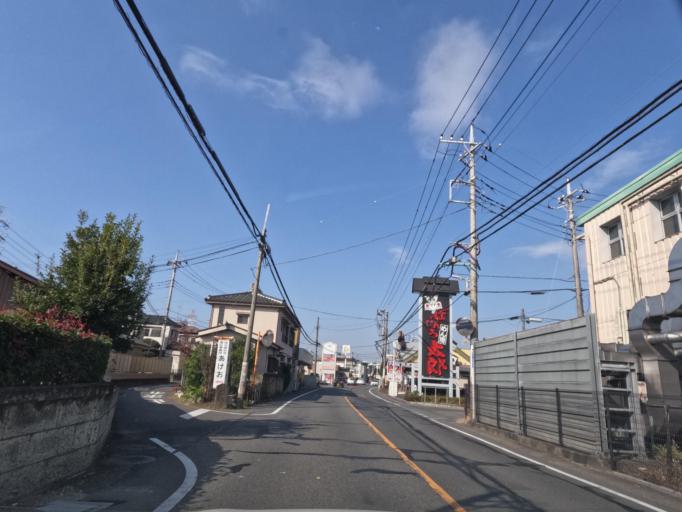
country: JP
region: Saitama
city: Ageoshimo
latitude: 35.9787
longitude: 139.6119
